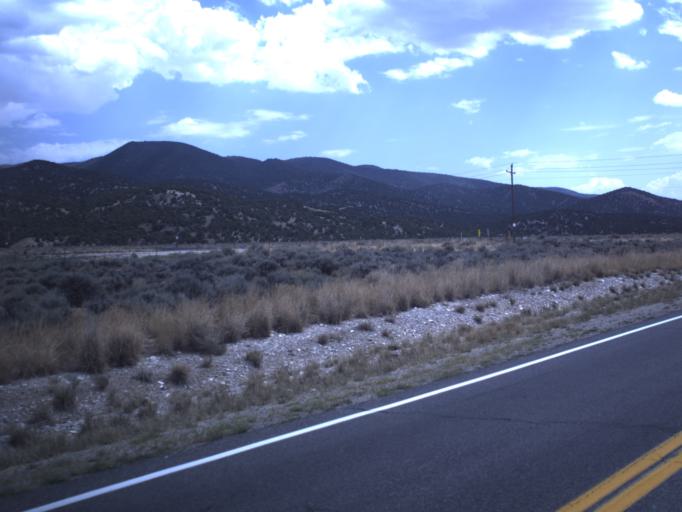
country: US
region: Utah
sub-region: Tooele County
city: Tooele
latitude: 40.3515
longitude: -112.3107
